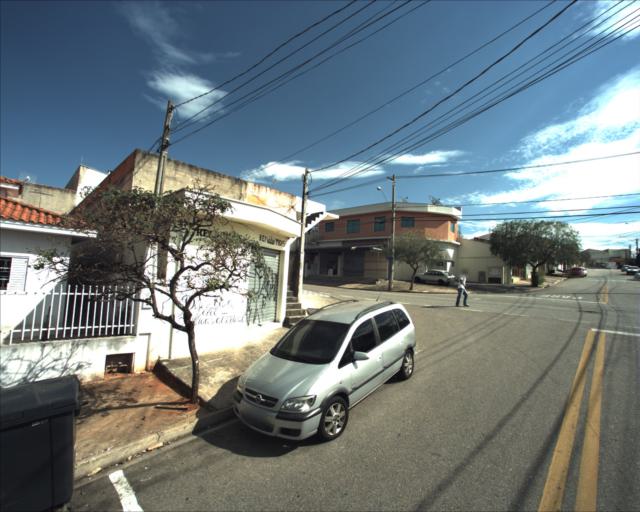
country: BR
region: Sao Paulo
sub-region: Sorocaba
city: Sorocaba
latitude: -23.4816
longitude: -47.5090
